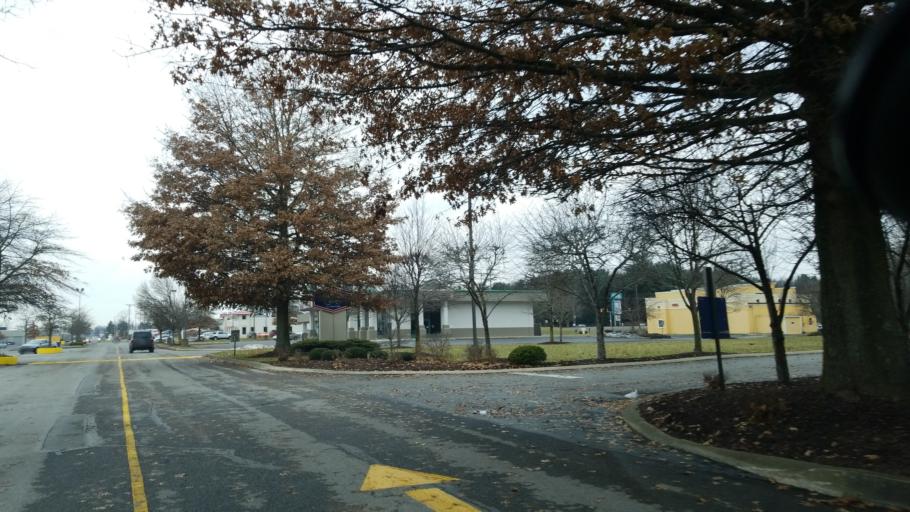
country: US
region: Pennsylvania
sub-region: Clearfield County
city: DuBois
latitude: 41.1209
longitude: -78.7231
